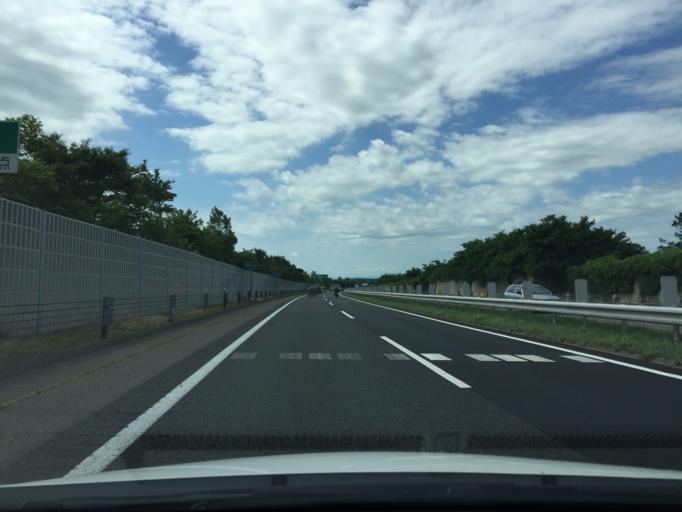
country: JP
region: Fukushima
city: Koriyama
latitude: 37.3833
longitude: 140.3128
